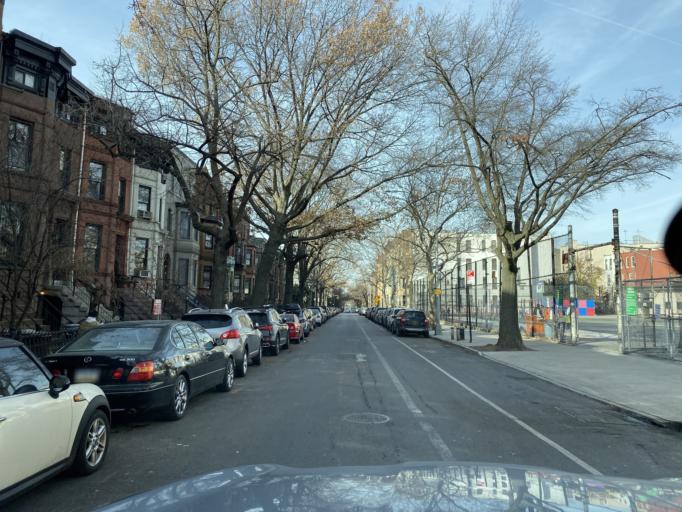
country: US
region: New York
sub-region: Kings County
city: Brooklyn
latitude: 40.6714
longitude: -73.9788
